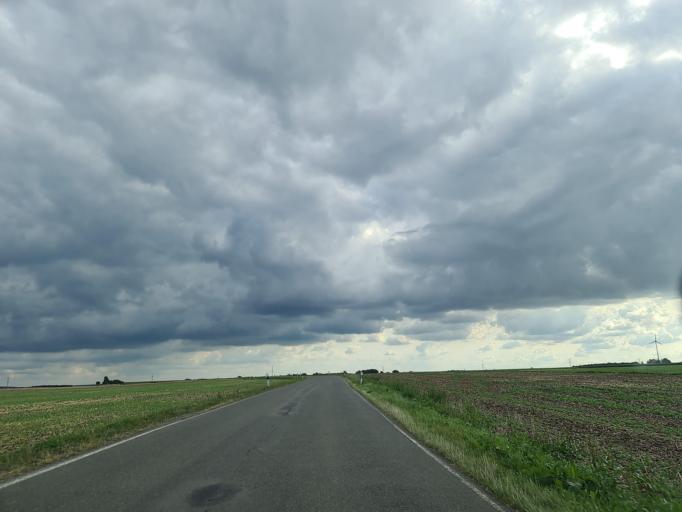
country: DE
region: Thuringia
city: Walpernhain
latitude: 51.0432
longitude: 11.9683
